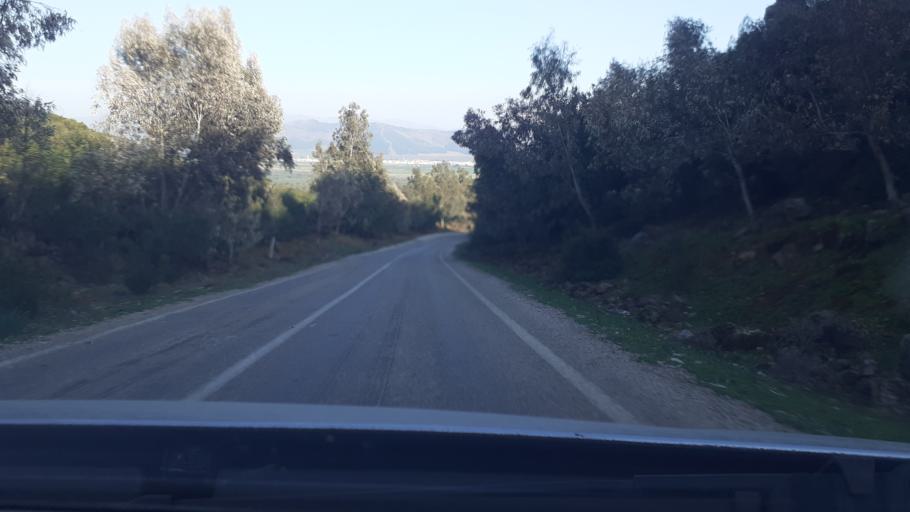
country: TR
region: Hatay
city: Aktepe
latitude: 36.7324
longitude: 36.4768
